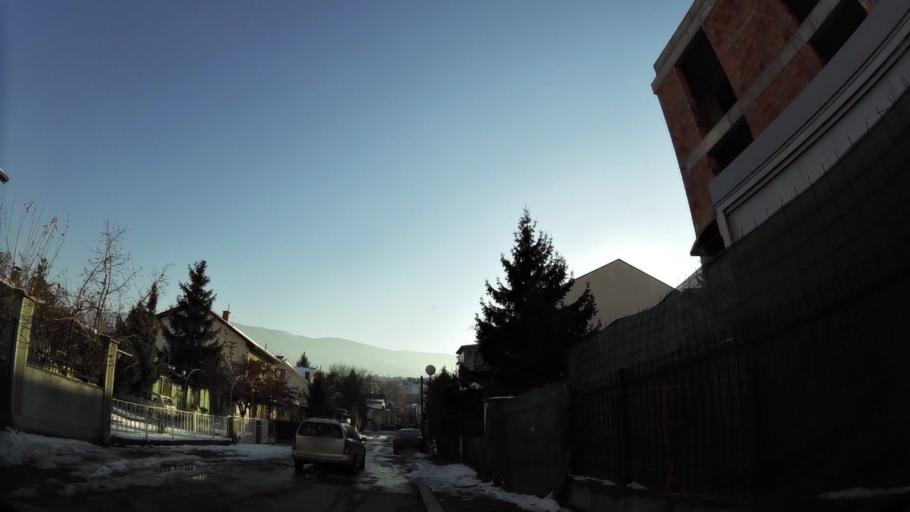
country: MK
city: Krushopek
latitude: 42.0013
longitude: 21.3846
